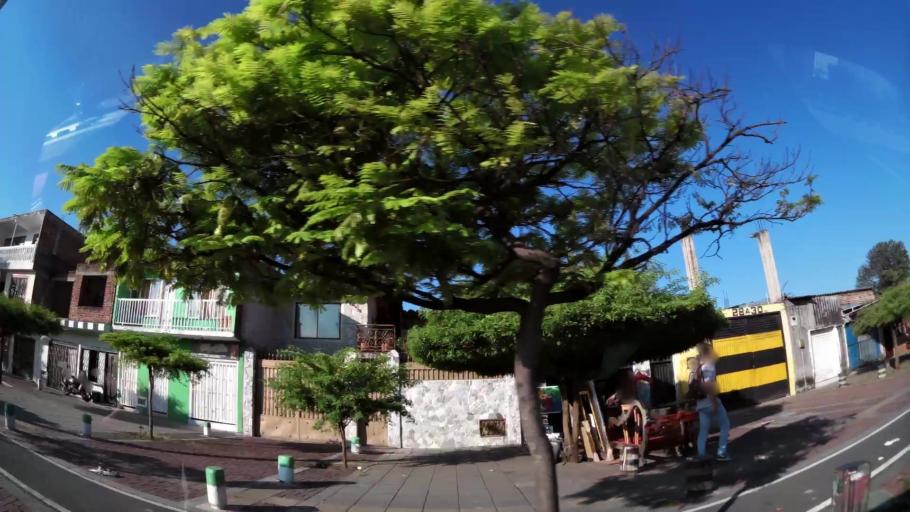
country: CO
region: Valle del Cauca
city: Cali
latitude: 3.4303
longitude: -76.5077
